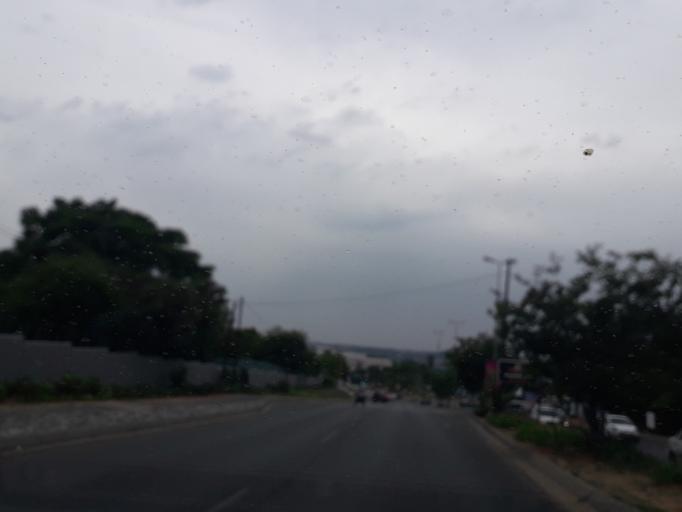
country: ZA
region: Gauteng
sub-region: West Rand District Municipality
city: Muldersdriseloop
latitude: -26.0620
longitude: 27.9516
